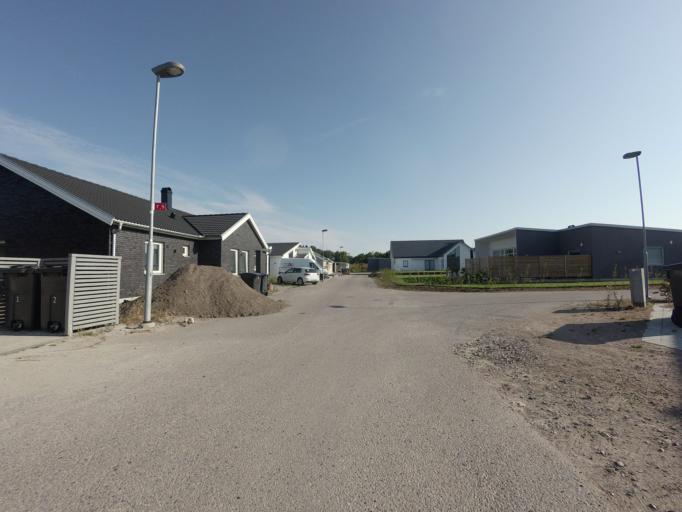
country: SE
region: Skane
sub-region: Trelleborgs Kommun
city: Trelleborg
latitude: 55.3665
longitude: 13.2086
